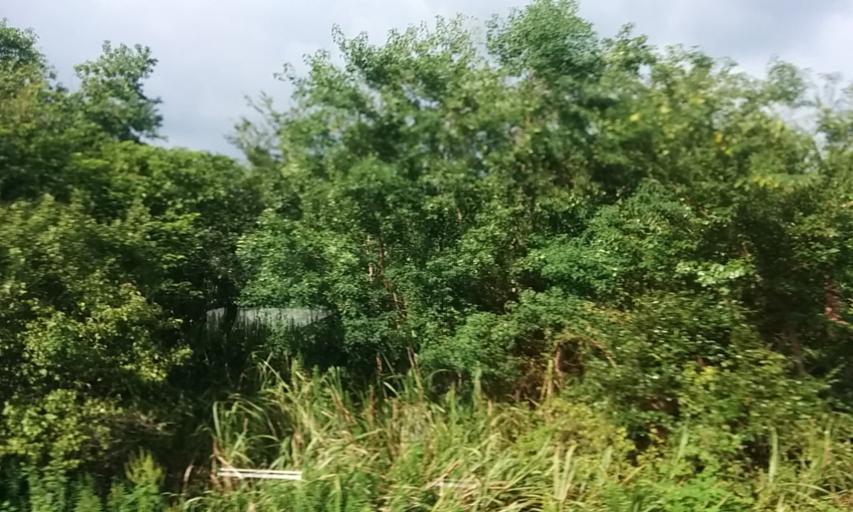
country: JP
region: Nara
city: Nara-shi
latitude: 34.6410
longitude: 135.7799
